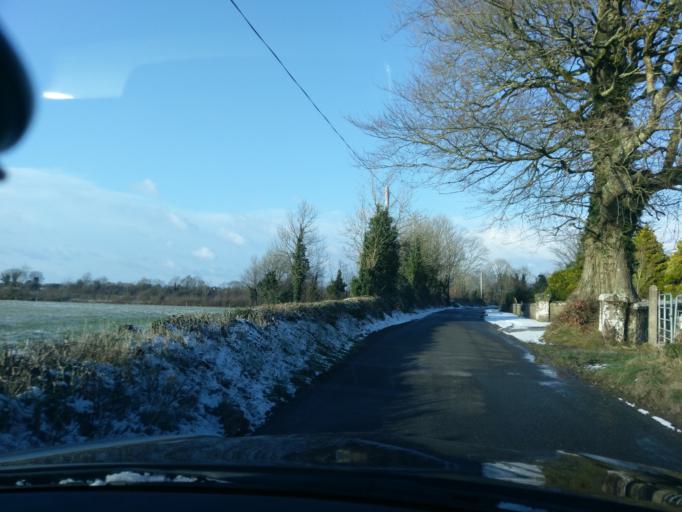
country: IE
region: Connaught
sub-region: County Galway
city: Athenry
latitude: 53.1830
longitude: -8.7273
